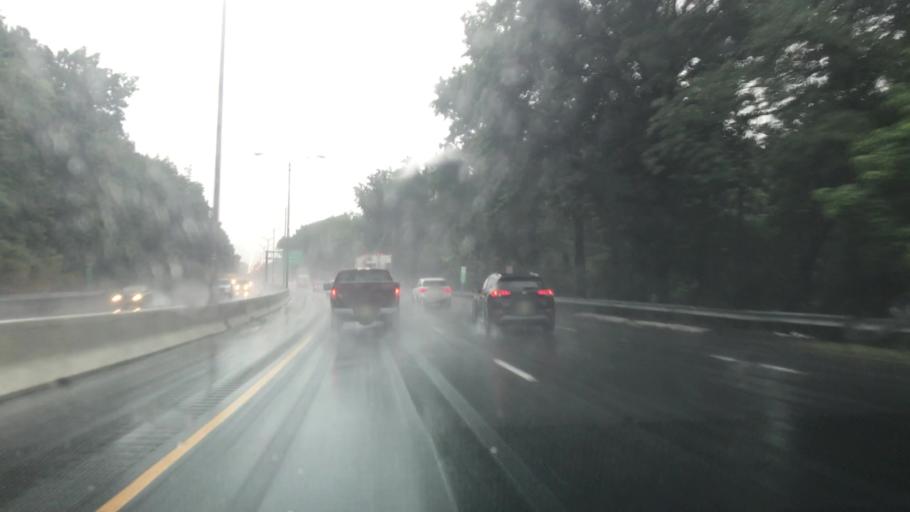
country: US
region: New Jersey
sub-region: Bergen County
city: Midland Park
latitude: 40.9823
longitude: -74.1620
